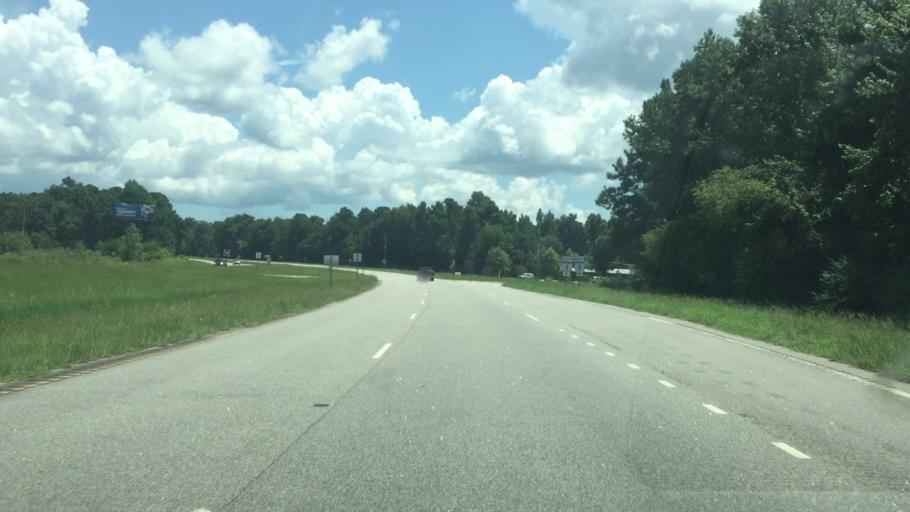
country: US
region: South Carolina
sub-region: Horry County
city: Loris
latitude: 34.0191
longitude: -78.7945
